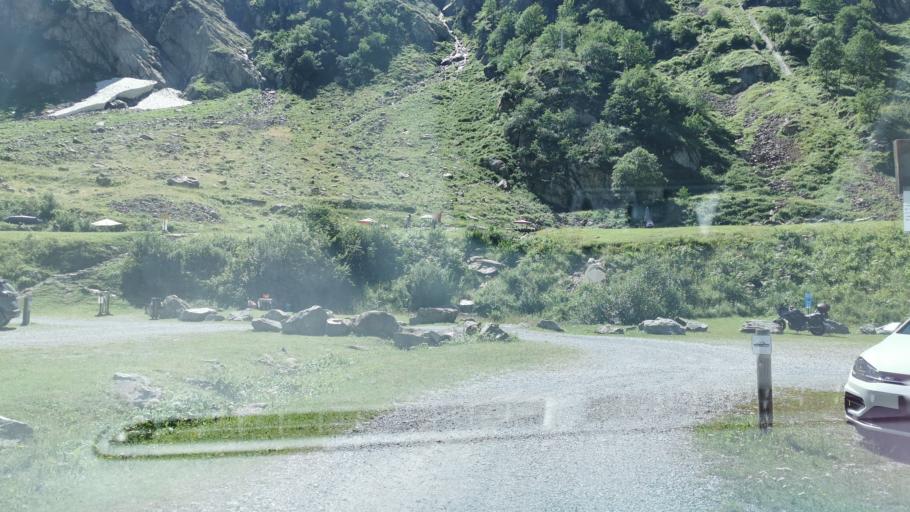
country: IT
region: Piedmont
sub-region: Provincia di Cuneo
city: Entracque
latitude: 44.1738
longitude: 7.3411
